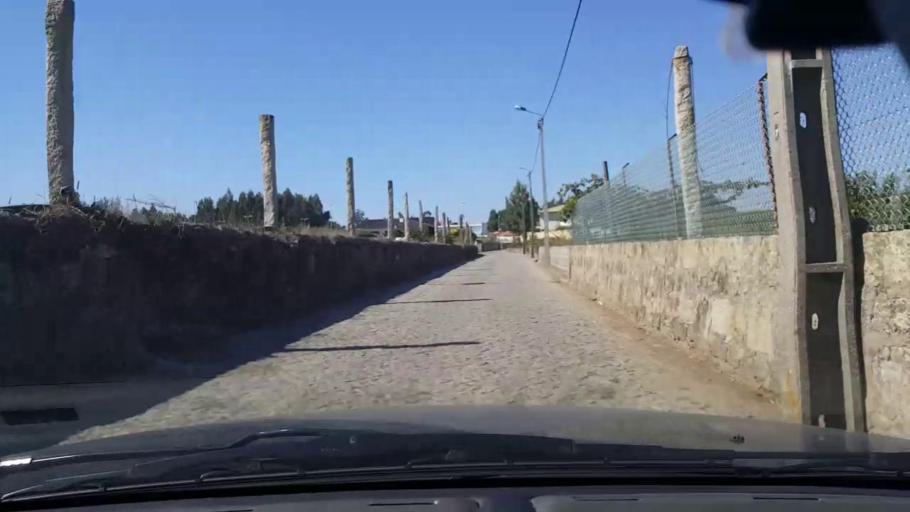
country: PT
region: Porto
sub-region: Matosinhos
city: Lavra
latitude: 41.2921
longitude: -8.6970
